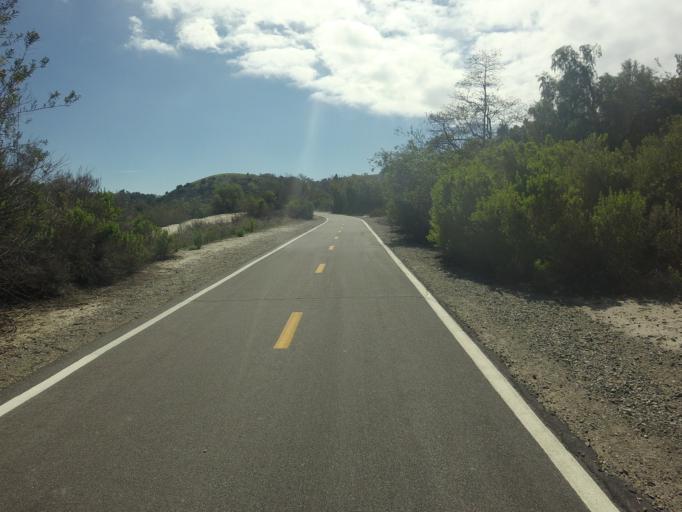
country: US
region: California
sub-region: Orange County
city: Aliso Viejo
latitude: 33.5544
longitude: -117.7193
